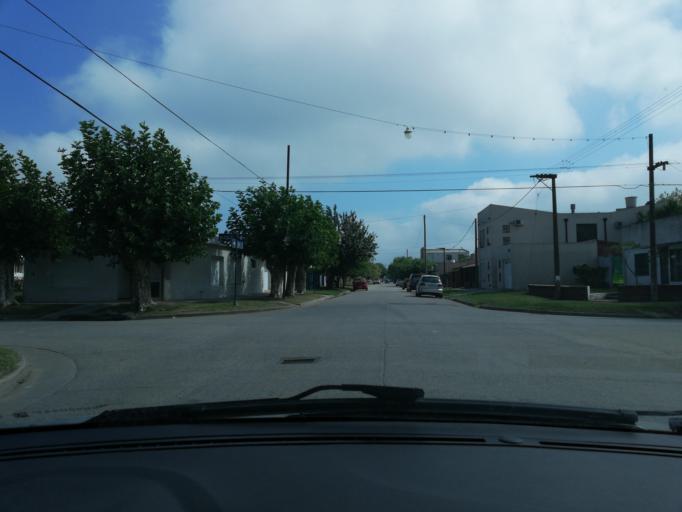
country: AR
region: Buenos Aires
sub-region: Partido de Balcarce
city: Balcarce
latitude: -37.8457
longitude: -58.2467
